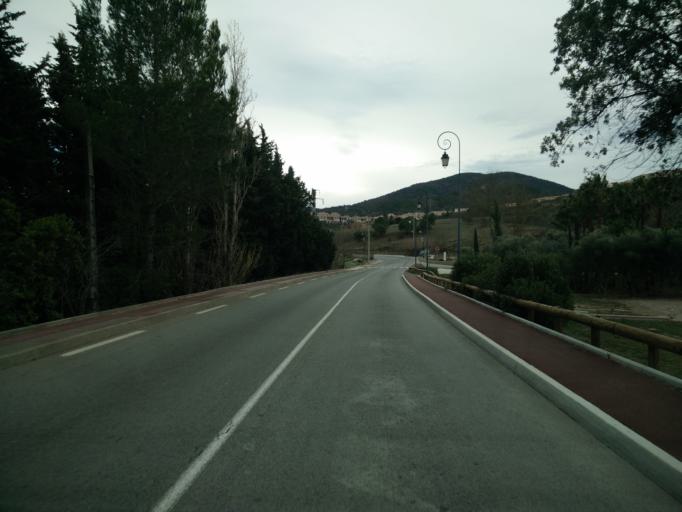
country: FR
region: Provence-Alpes-Cote d'Azur
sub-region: Departement du Var
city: Roquebrune-sur-Argens
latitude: 43.4487
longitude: 6.6331
